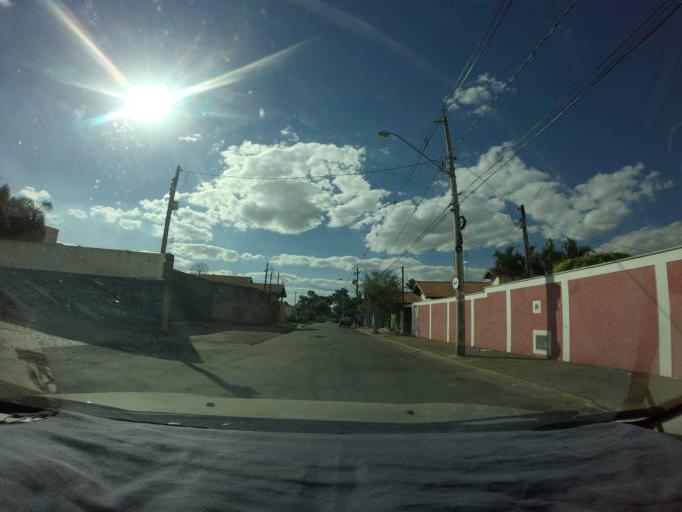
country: BR
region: Sao Paulo
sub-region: Piracicaba
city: Piracicaba
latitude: -22.7398
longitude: -47.5950
